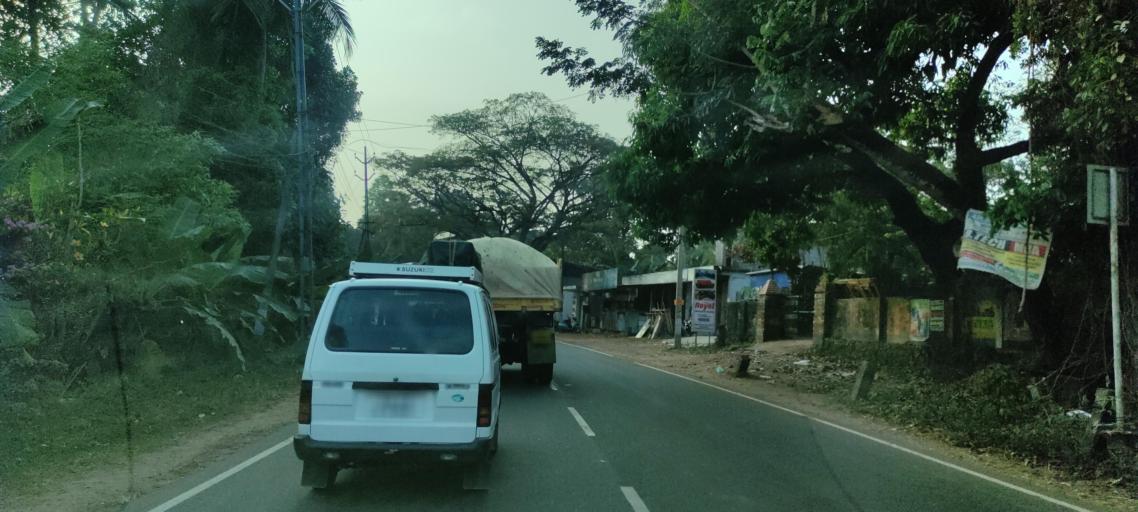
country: IN
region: Kerala
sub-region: Alappuzha
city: Kattanam
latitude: 9.1757
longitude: 76.6156
